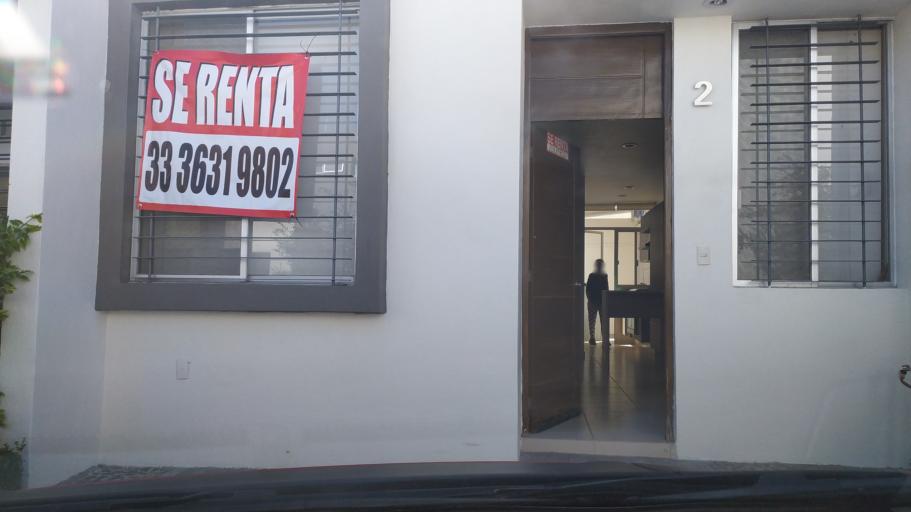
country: MX
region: Jalisco
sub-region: Tlajomulco de Zuniga
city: Palomar
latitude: 20.6298
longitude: -103.4641
